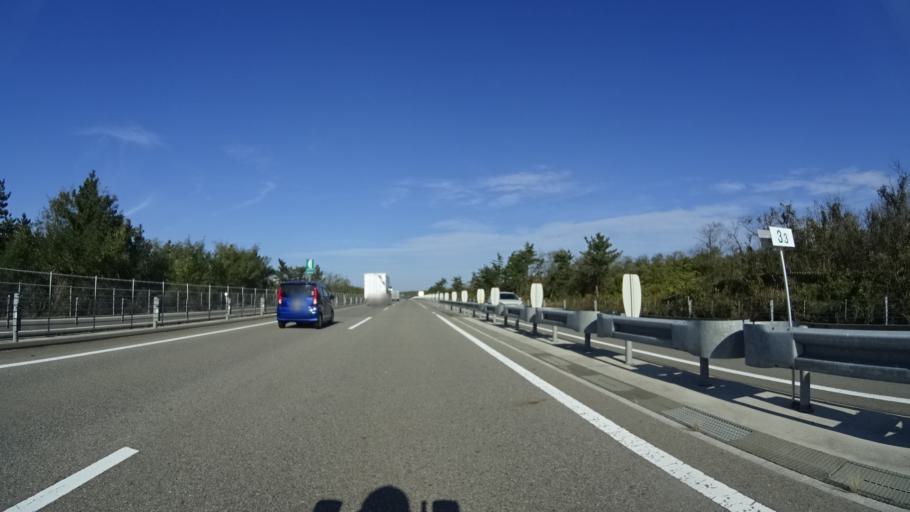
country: JP
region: Ishikawa
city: Kanazawa-shi
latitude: 36.6572
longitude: 136.6396
